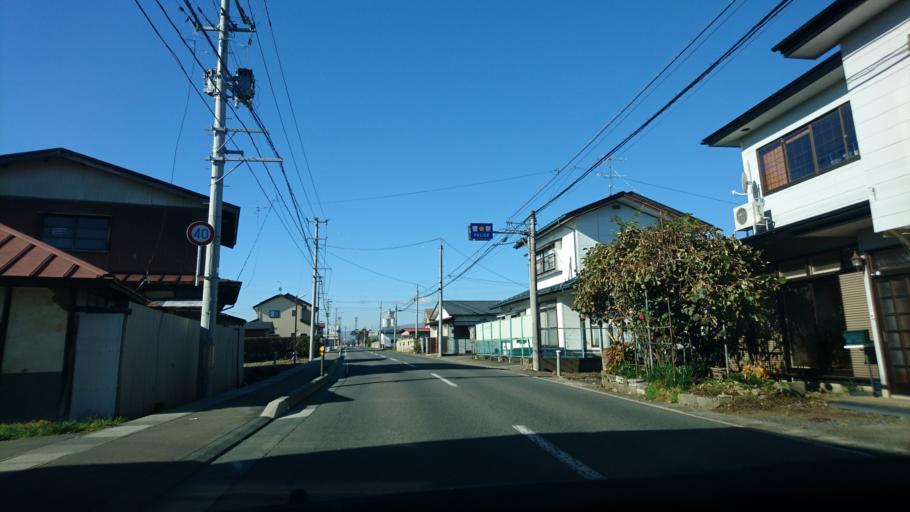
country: JP
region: Iwate
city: Mizusawa
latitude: 39.1409
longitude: 141.0893
